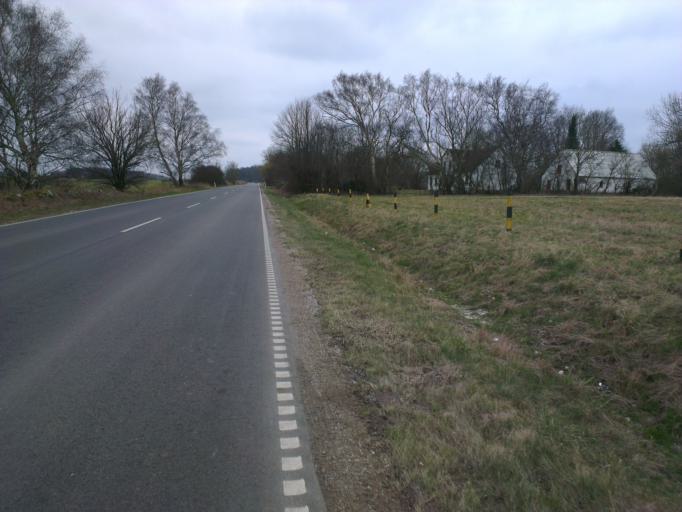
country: DK
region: Capital Region
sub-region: Frederikssund Kommune
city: Jaegerspris
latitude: 55.8827
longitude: 11.9550
